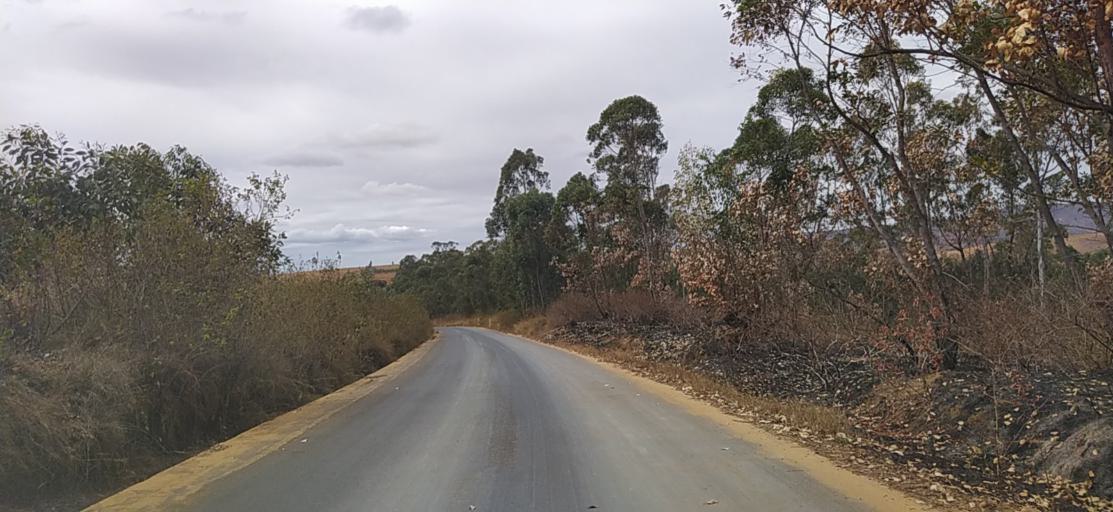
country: MG
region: Alaotra Mangoro
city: Ambatondrazaka
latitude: -17.9345
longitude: 48.2512
